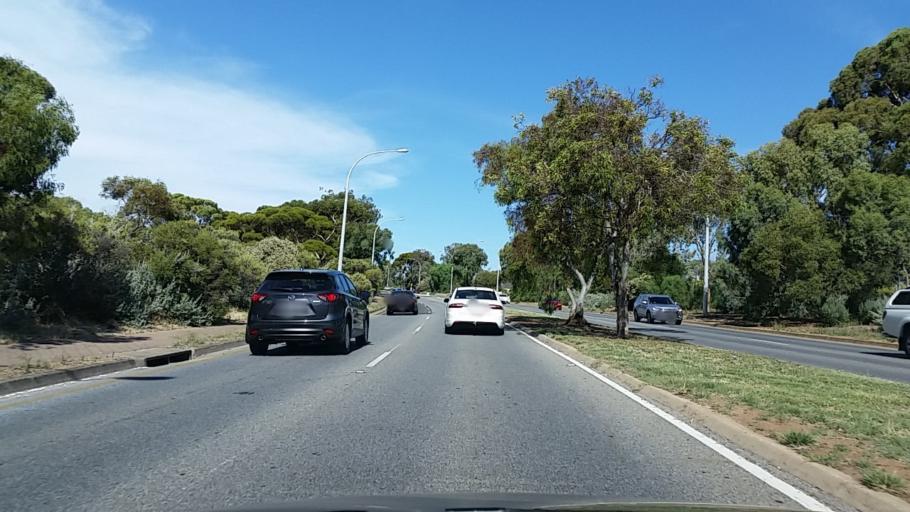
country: AU
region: South Australia
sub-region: Port Adelaide Enfield
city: Gilles Plains
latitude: -34.8297
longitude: 138.6549
